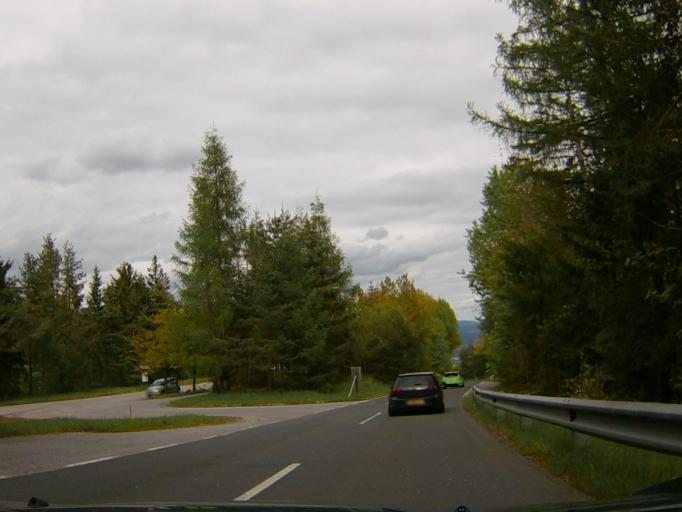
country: AT
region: Carinthia
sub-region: Villach Stadt
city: Villach
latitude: 46.5995
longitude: 13.8048
